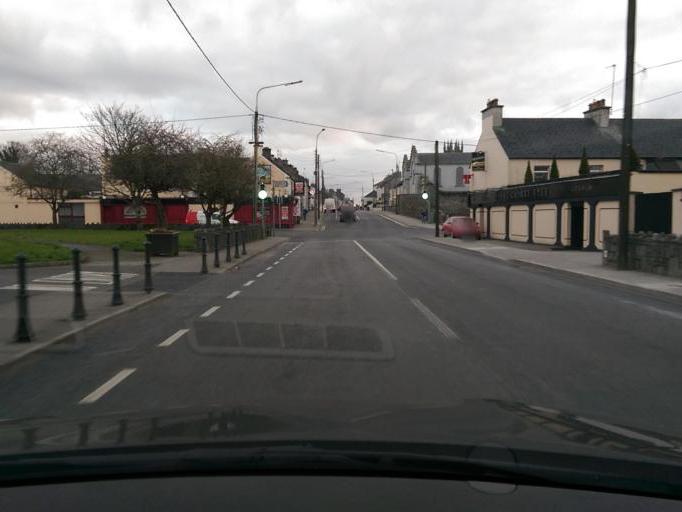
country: IE
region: Leinster
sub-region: Uibh Fhaili
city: Birr
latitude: 53.1004
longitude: -7.9084
